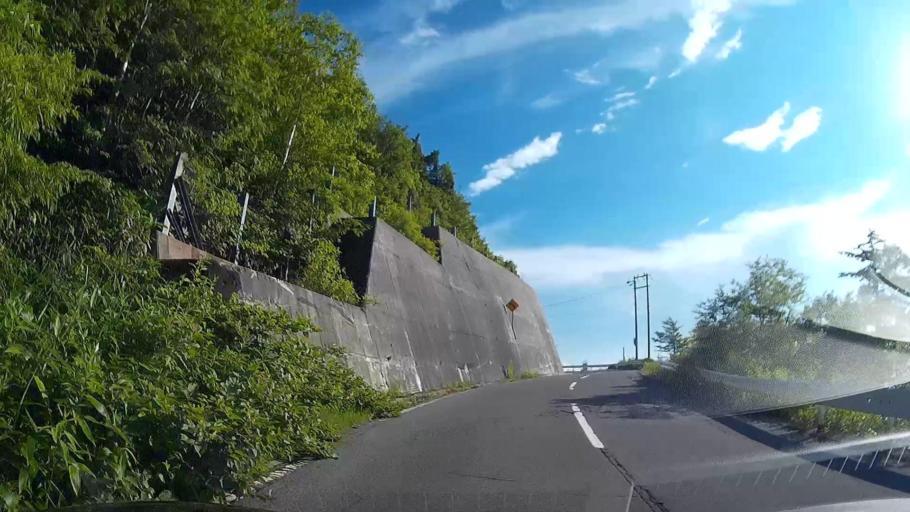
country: JP
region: Nagano
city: Nakano
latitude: 36.6399
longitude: 138.5261
